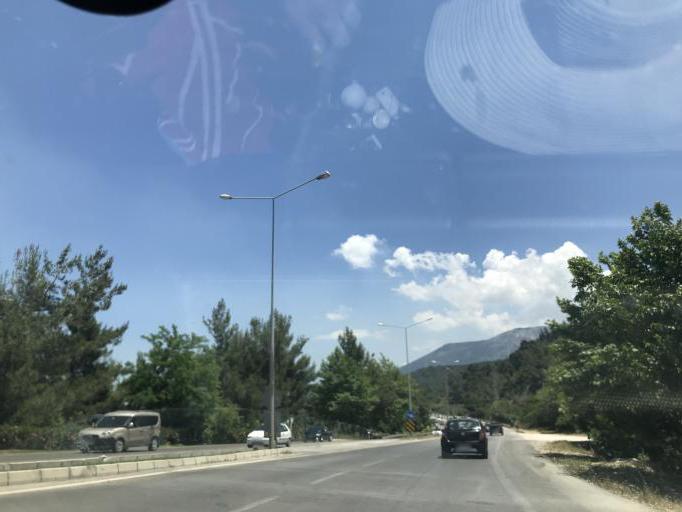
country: TR
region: Denizli
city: Denizli
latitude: 37.7313
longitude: 29.1585
